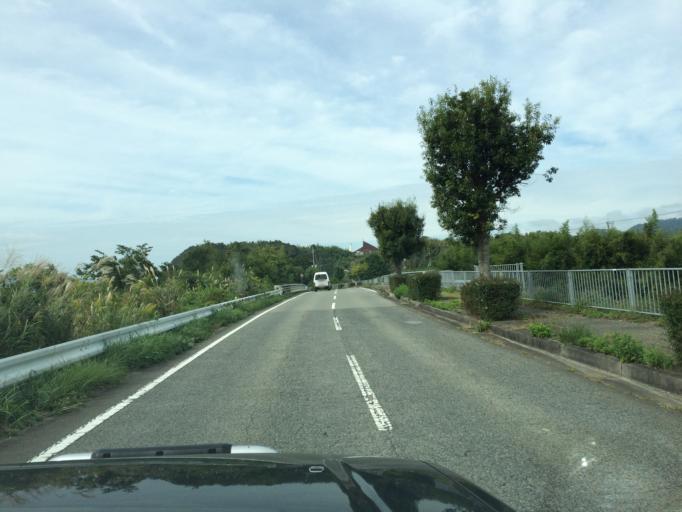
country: JP
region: Hyogo
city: Sasayama
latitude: 35.0736
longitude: 135.2576
